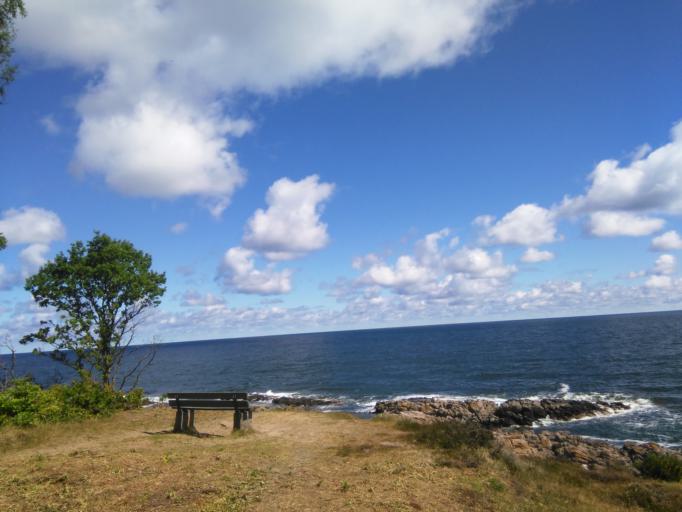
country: DK
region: Capital Region
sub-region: Bornholm Kommune
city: Ronne
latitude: 55.2961
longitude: 14.7771
